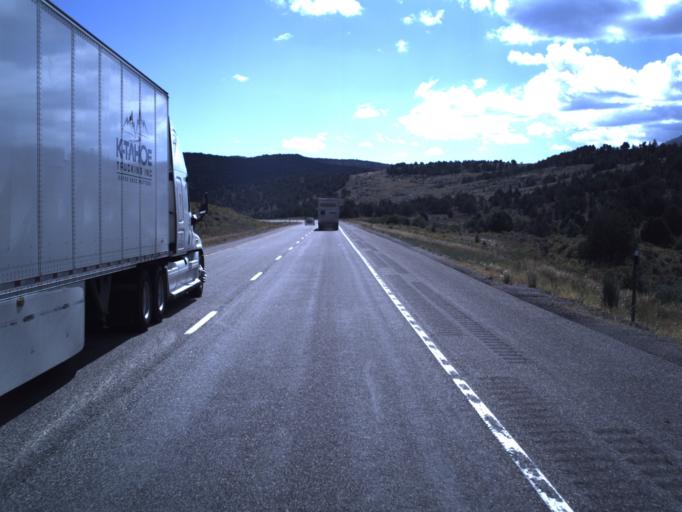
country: US
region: Utah
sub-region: Sevier County
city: Salina
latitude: 38.8565
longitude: -111.5512
